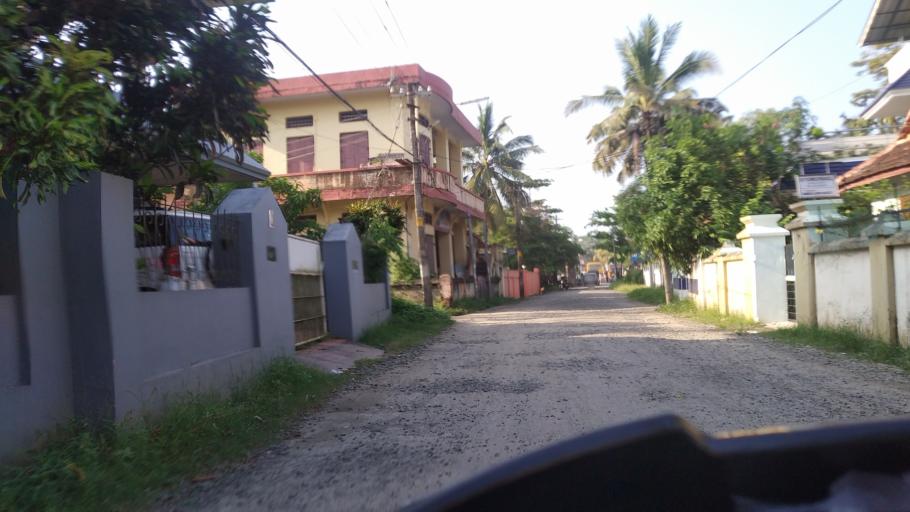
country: IN
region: Kerala
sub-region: Ernakulam
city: Elur
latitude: 10.0466
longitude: 76.2205
